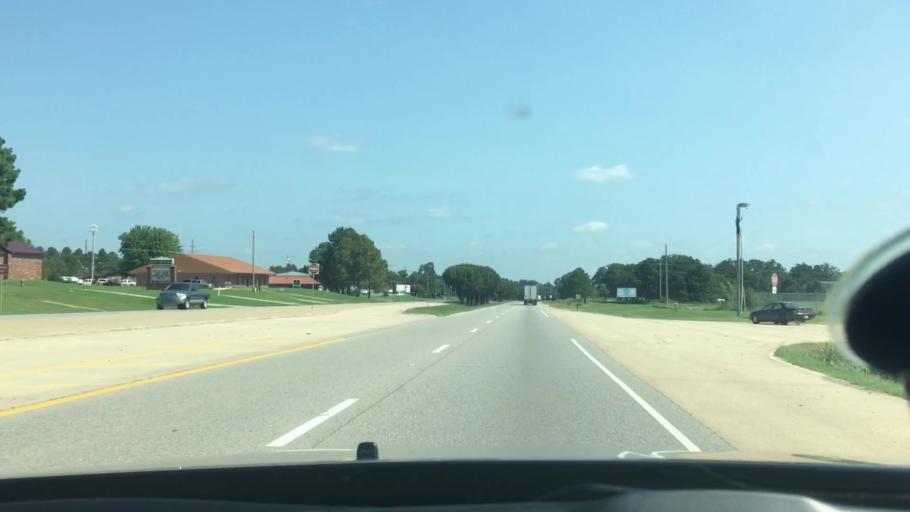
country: US
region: Oklahoma
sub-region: Atoka County
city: Atoka
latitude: 34.3529
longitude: -96.1481
